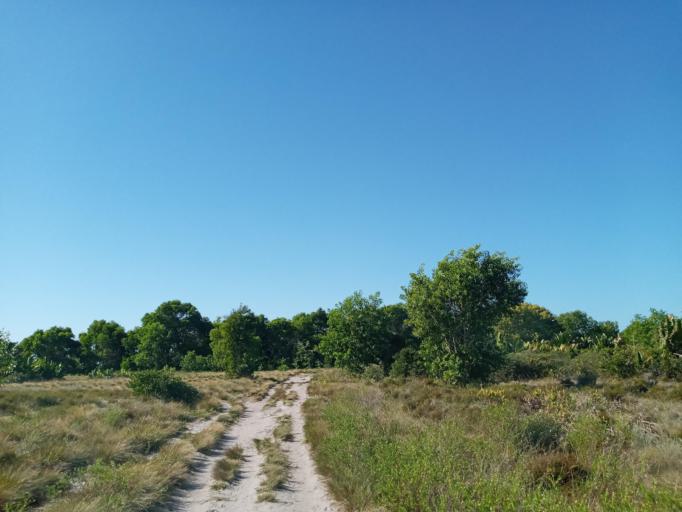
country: MG
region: Anosy
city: Fort Dauphin
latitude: -24.9054
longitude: 47.0995
